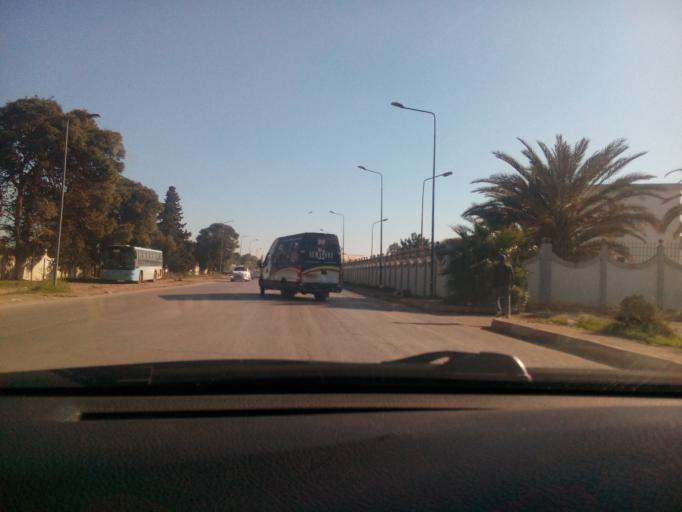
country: DZ
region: Oran
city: Es Senia
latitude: 35.6387
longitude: -0.6126
